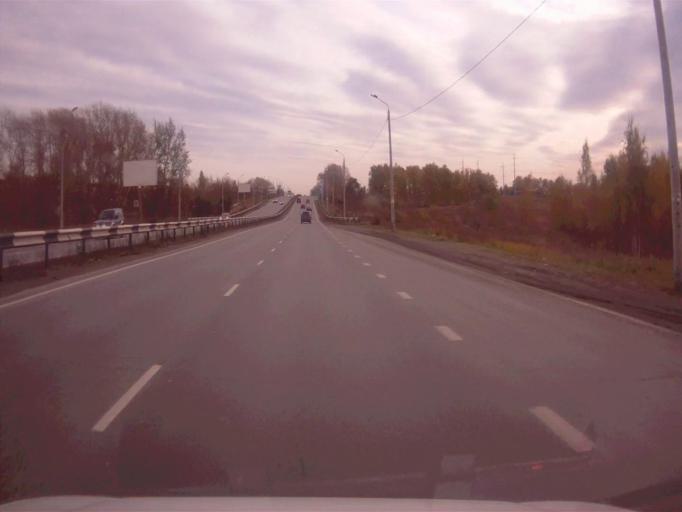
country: RU
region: Chelyabinsk
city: Novosineglazovskiy
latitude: 55.0590
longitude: 61.4034
